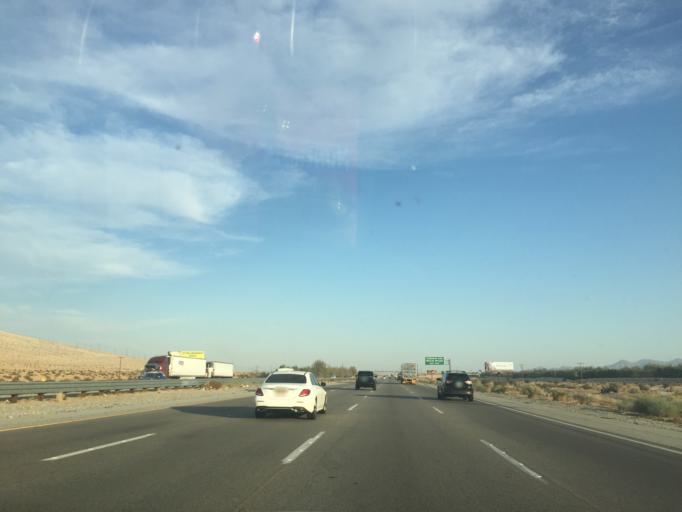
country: US
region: California
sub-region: Riverside County
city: Desert Edge
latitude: 33.8567
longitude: -116.4712
